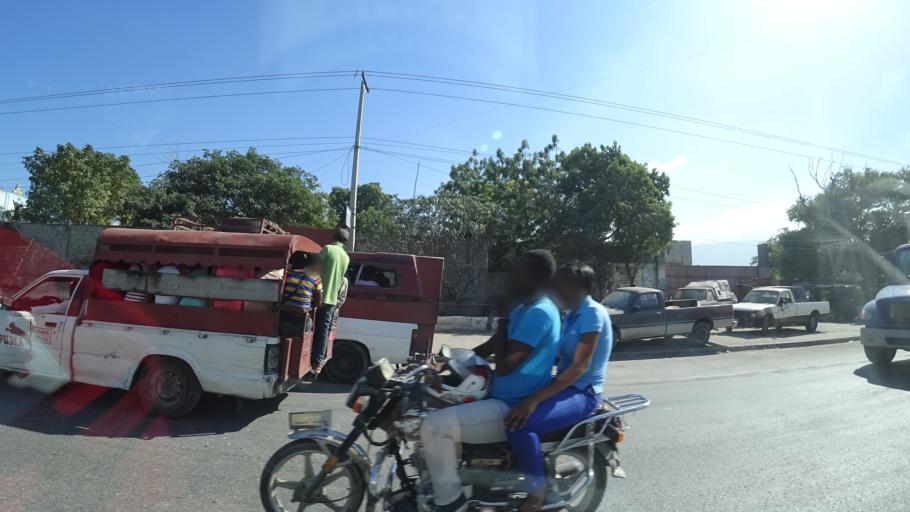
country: HT
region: Ouest
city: Delmas 73
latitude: 18.5797
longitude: -72.3136
